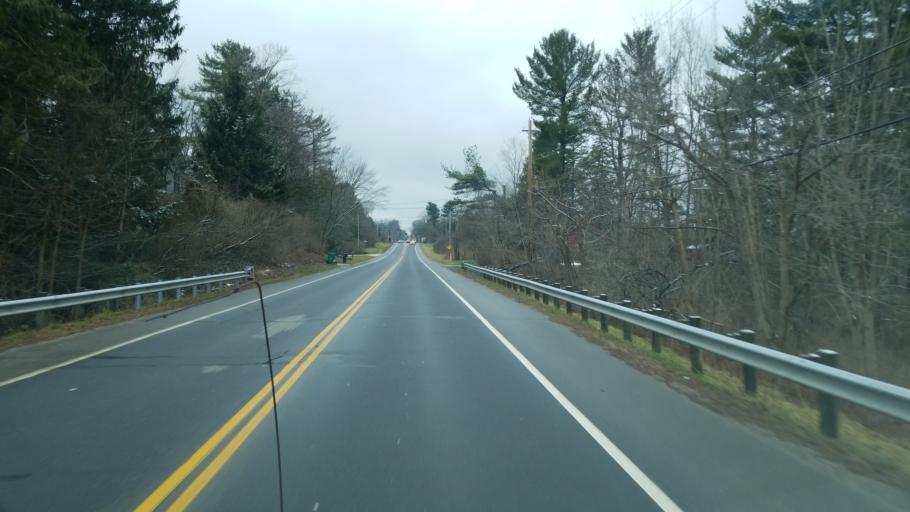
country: US
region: Ohio
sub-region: Summit County
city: Hudson
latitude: 41.2398
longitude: -81.4057
